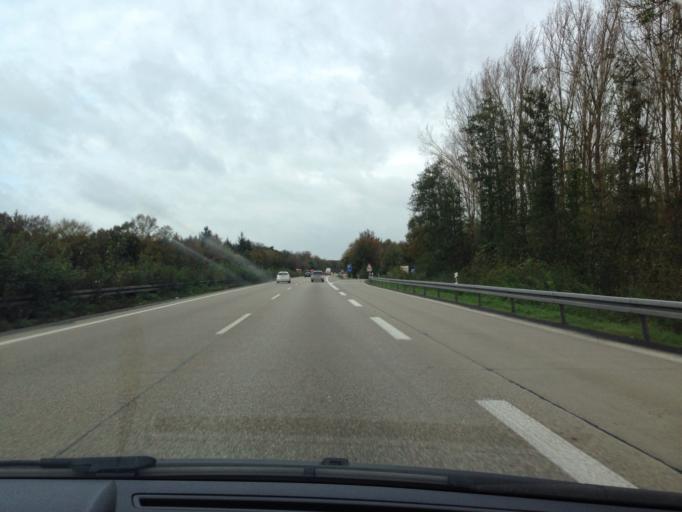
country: DE
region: North Rhine-Westphalia
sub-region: Regierungsbezirk Munster
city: Ascheberg
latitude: 51.8394
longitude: 7.5883
